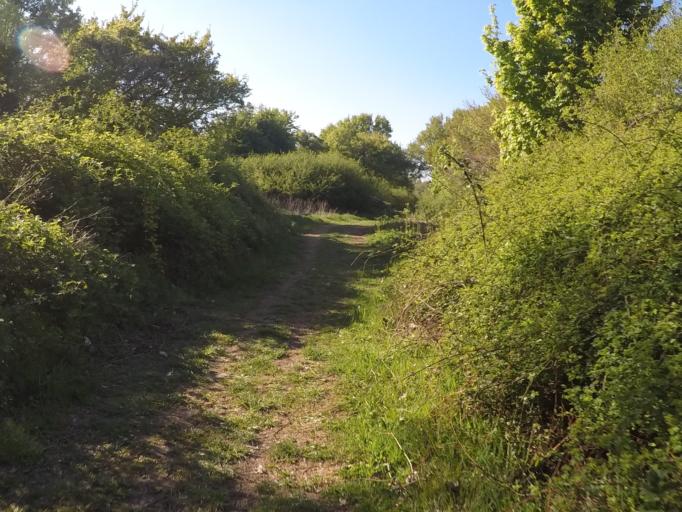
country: GB
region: England
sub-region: Oxfordshire
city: Stonesfield
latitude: 51.8738
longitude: -1.4452
